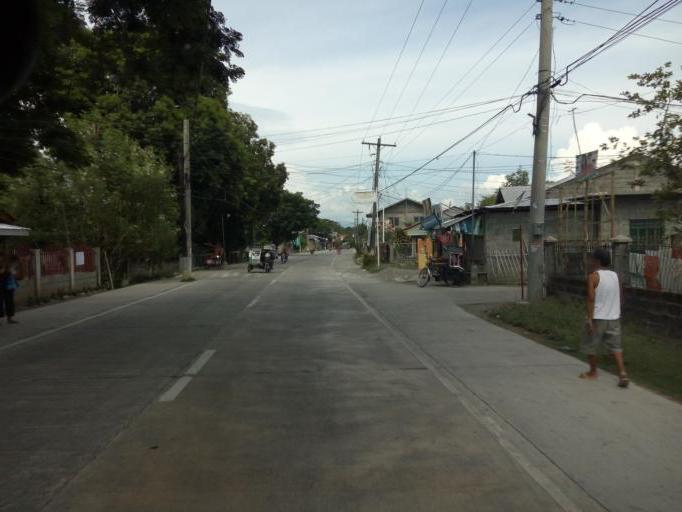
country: PH
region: Ilocos
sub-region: Province of Pangasinan
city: Rosales
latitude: 15.8963
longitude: 120.6434
